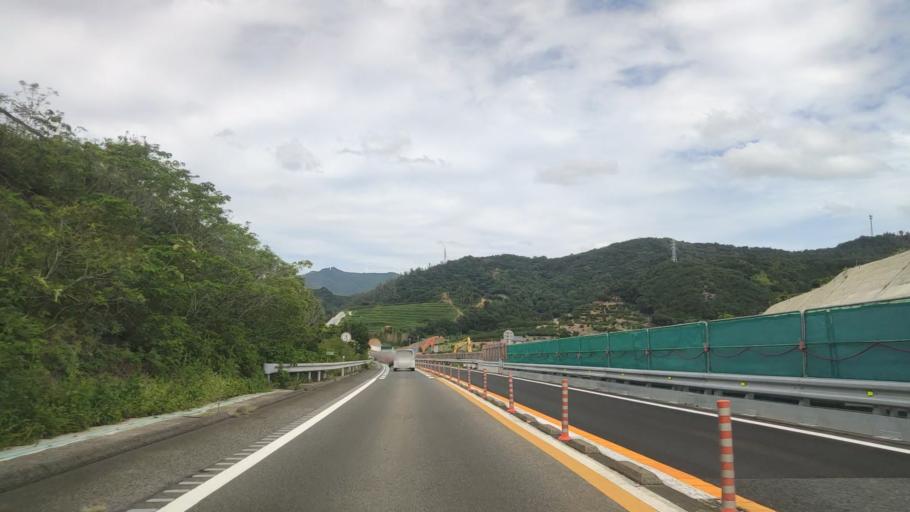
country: JP
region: Wakayama
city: Gobo
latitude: 33.9120
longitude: 135.1944
